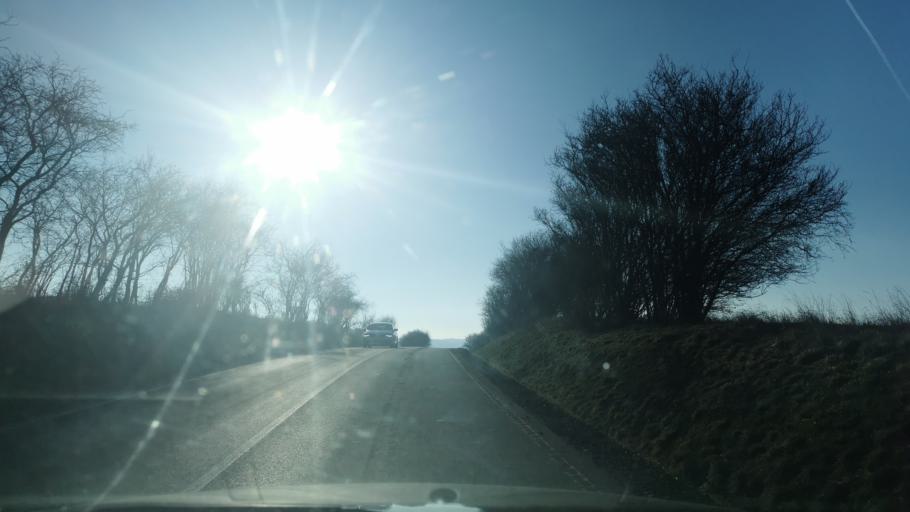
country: SK
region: Trnavsky
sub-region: Okres Senica
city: Senica
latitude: 48.7490
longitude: 17.3496
